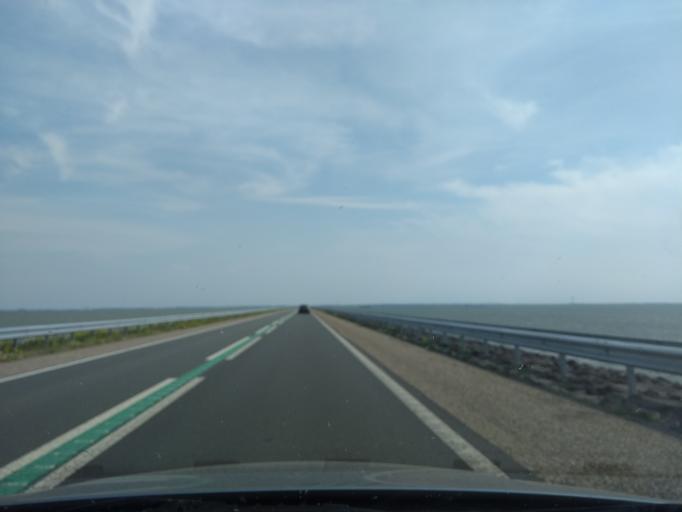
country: NL
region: Flevoland
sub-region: Gemeente Lelystad
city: Lelystad
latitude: 52.6259
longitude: 5.4230
